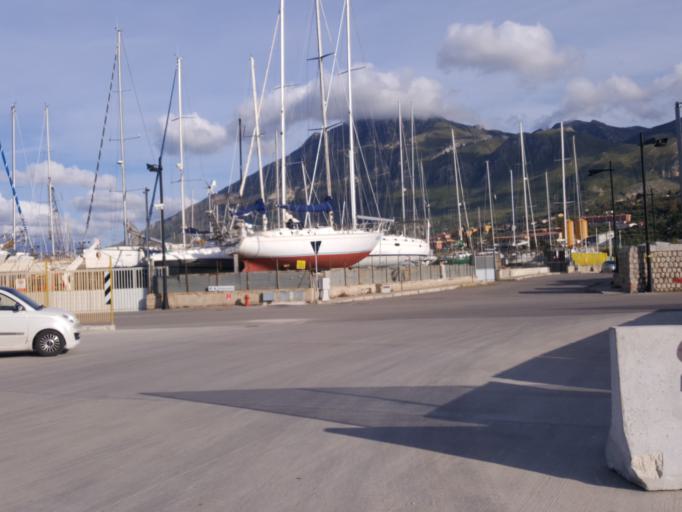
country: IT
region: Sicily
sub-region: Palermo
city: Termini Imerese
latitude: 37.9857
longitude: 13.7038
